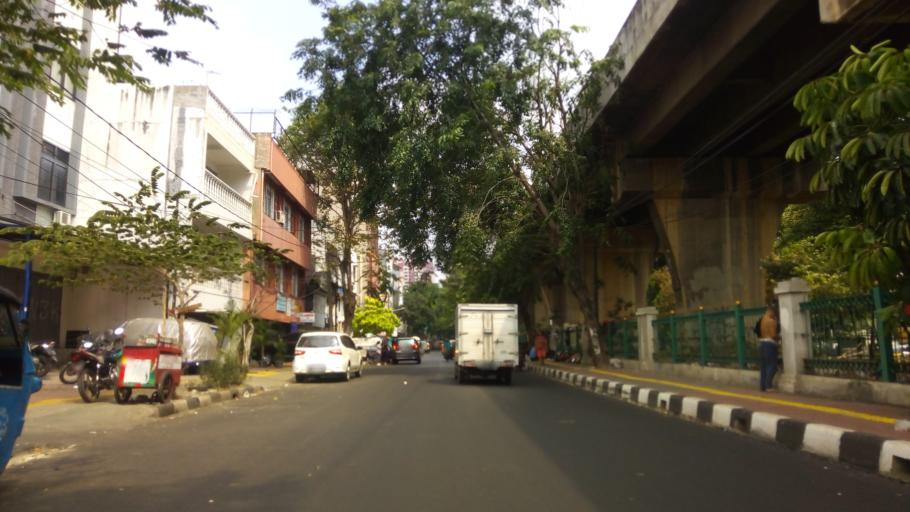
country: ID
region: Jakarta Raya
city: Jakarta
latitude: -6.1575
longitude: 106.8275
